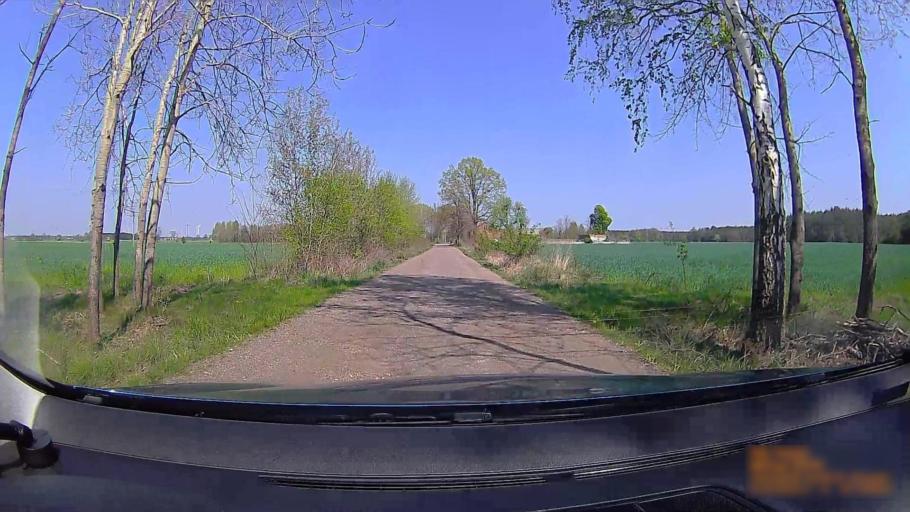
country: PL
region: Greater Poland Voivodeship
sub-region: Powiat koninski
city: Rychwal
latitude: 52.0929
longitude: 18.1830
